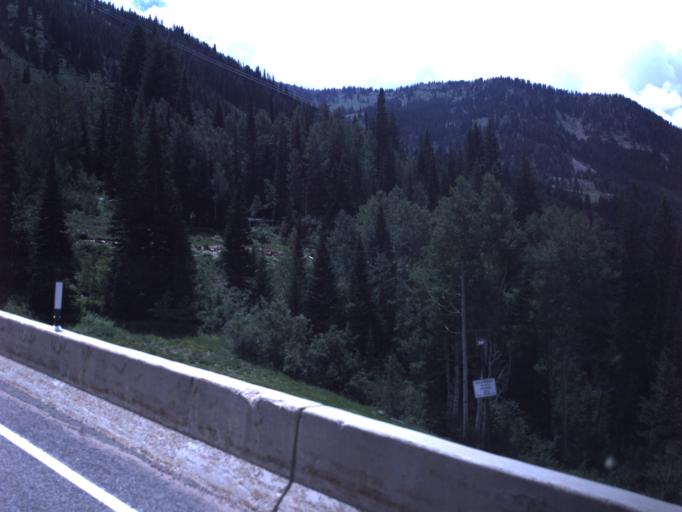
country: US
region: Utah
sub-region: Salt Lake County
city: Granite
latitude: 40.5827
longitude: -111.6529
